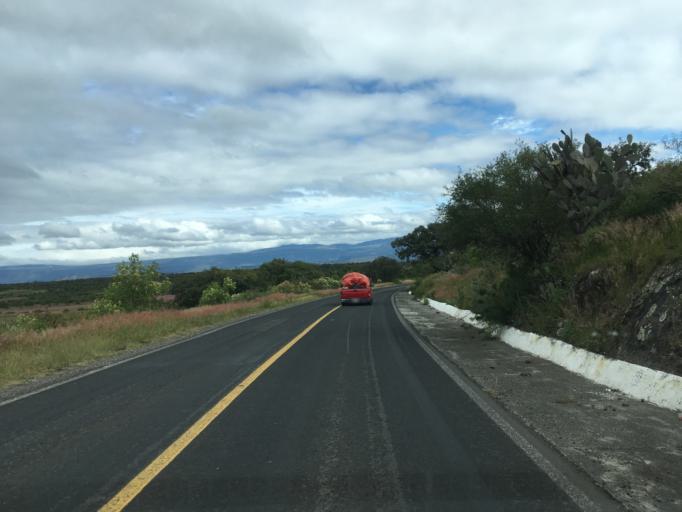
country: MX
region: Hidalgo
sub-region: Atotonilco el Grande
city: Santa Maria Amajac
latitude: 20.4099
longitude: -98.7054
